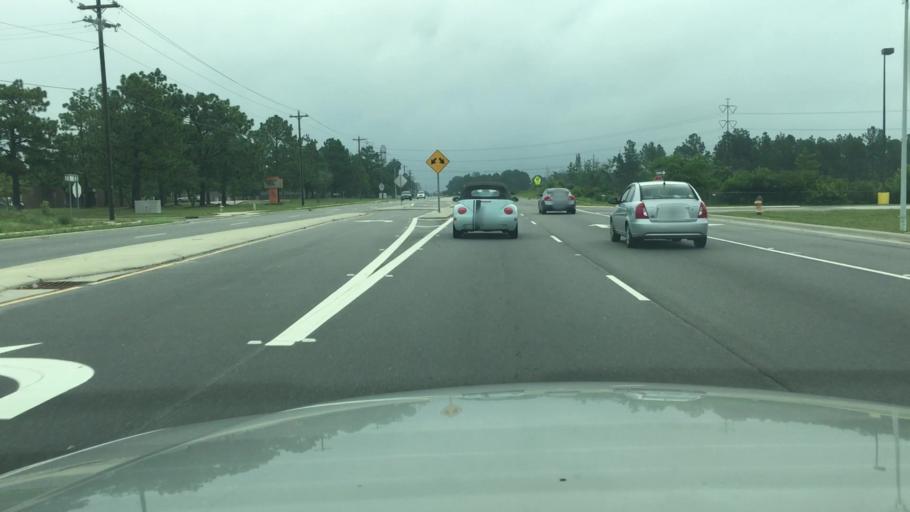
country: US
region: North Carolina
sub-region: Cumberland County
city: Hope Mills
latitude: 35.0049
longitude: -78.9150
